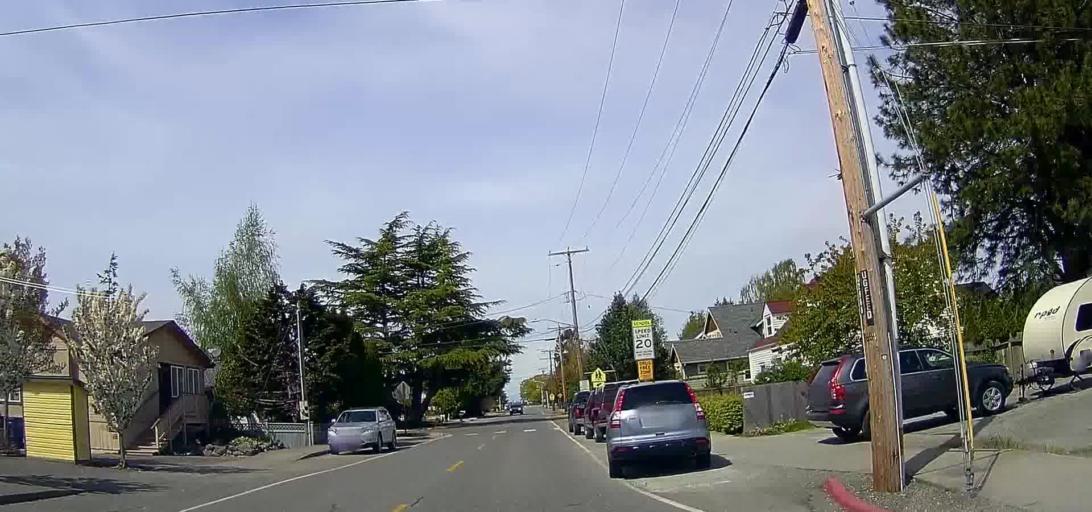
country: US
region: Washington
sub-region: Skagit County
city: Mount Vernon
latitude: 48.3925
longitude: -122.4904
